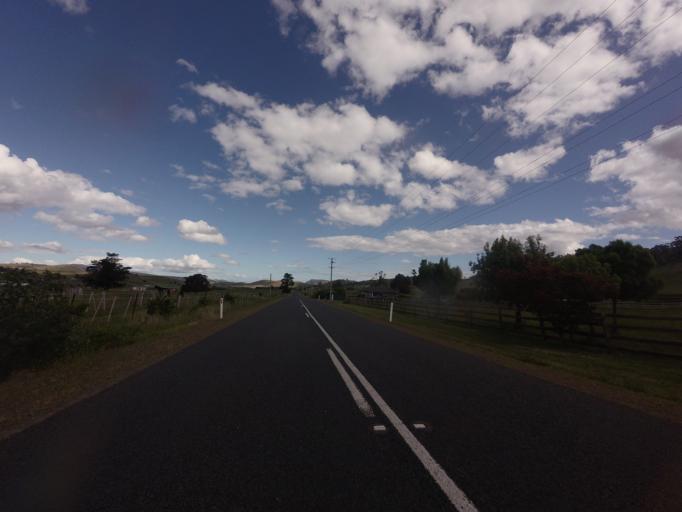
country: AU
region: Tasmania
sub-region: Brighton
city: Bridgewater
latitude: -42.5190
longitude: 147.3544
